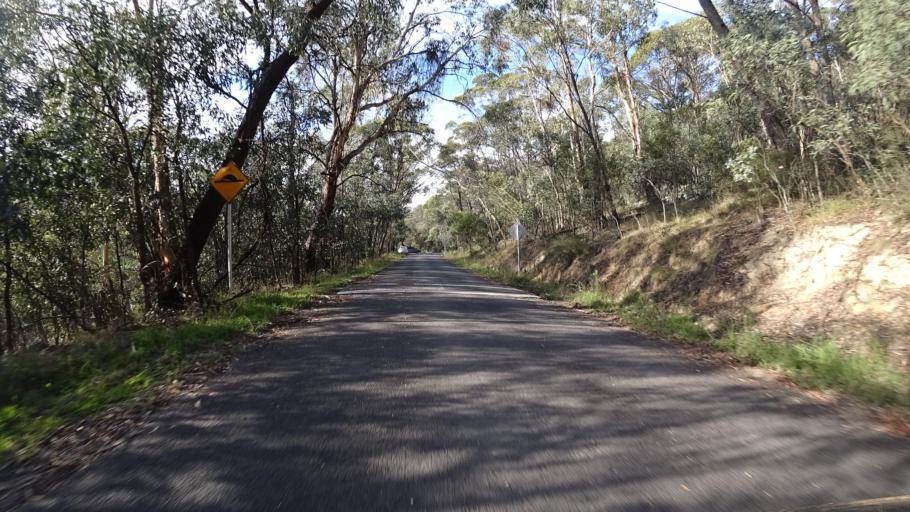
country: AU
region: New South Wales
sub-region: Lithgow
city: Lithgow
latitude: -33.4946
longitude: 150.1501
